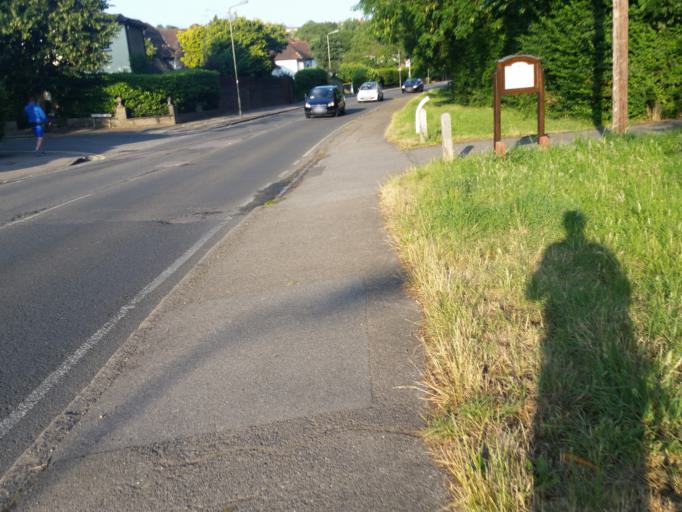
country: GB
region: England
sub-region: Greater London
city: Barnet
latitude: 51.6309
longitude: -0.1846
